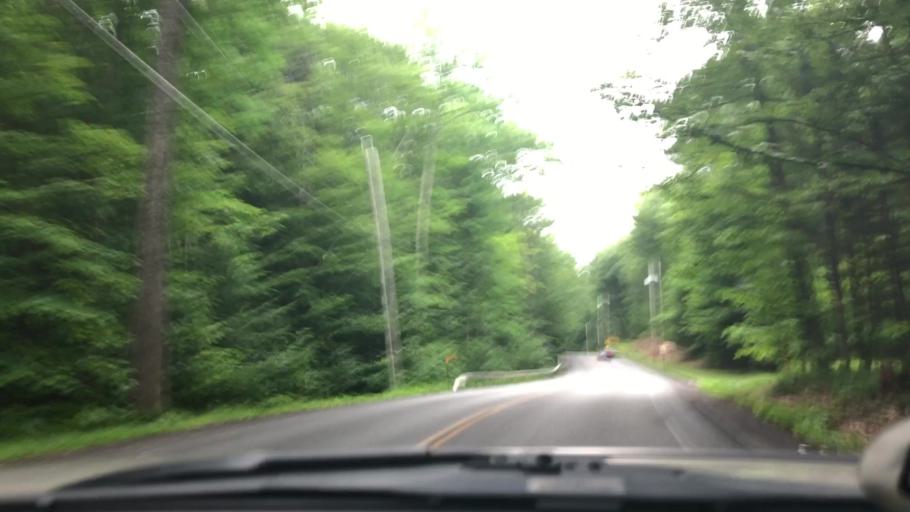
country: US
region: New York
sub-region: Saratoga County
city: Corinth
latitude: 43.1927
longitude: -73.7552
